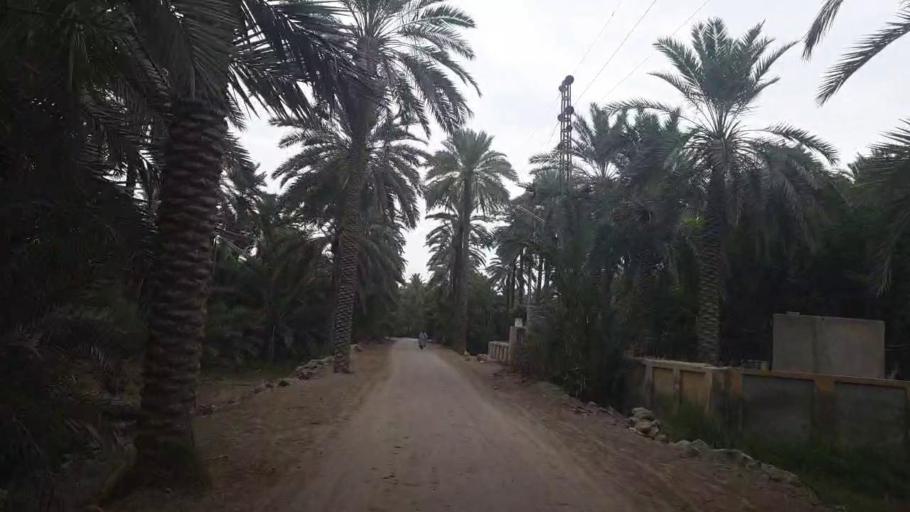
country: PK
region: Sindh
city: Khairpur
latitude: 27.5734
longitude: 68.7447
